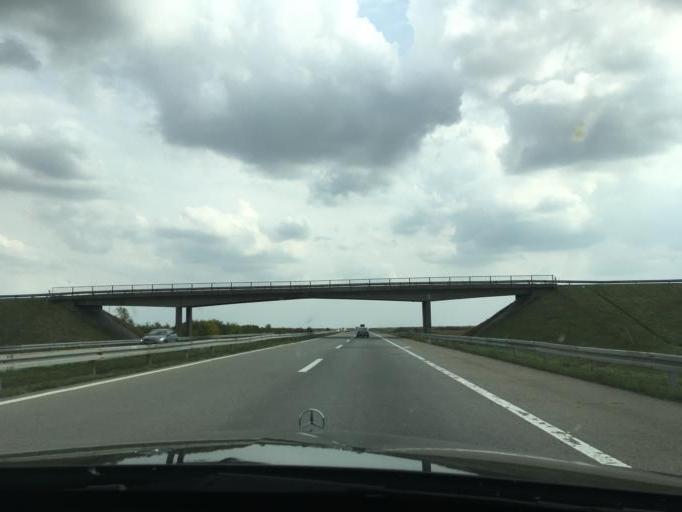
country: RS
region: Autonomna Pokrajina Vojvodina
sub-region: Sremski Okrug
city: Pecinci
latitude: 44.9052
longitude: 20.0051
